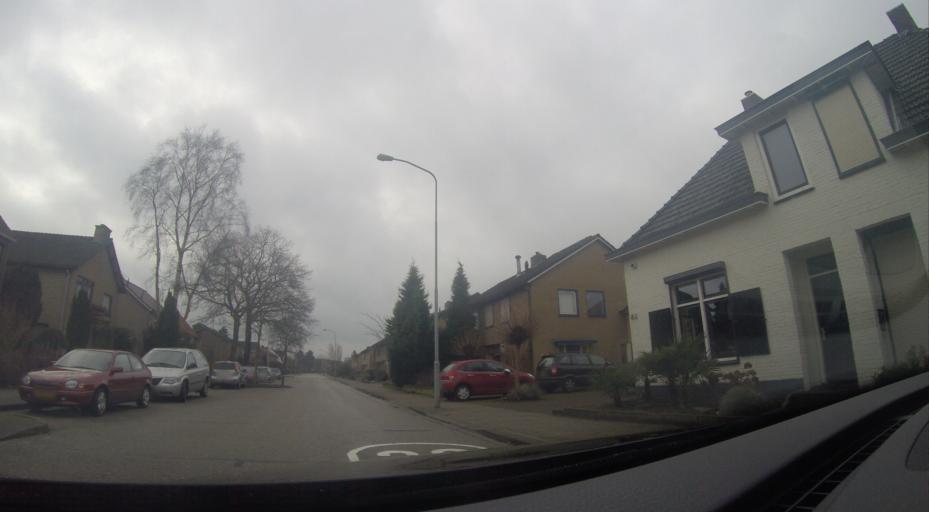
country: NL
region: Gelderland
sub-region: Gemeente Doetinchem
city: Doetinchem
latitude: 51.9650
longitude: 6.3109
